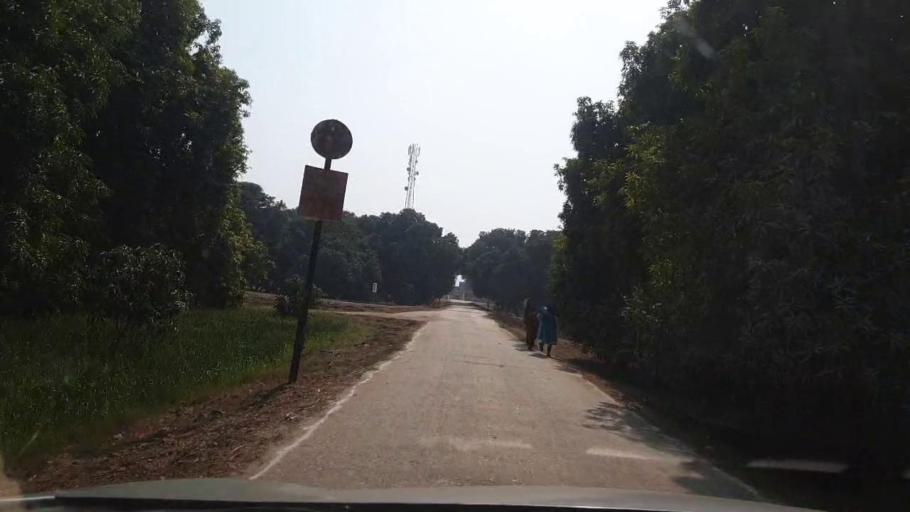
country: PK
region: Sindh
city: Tando Allahyar
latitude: 25.4803
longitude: 68.7718
